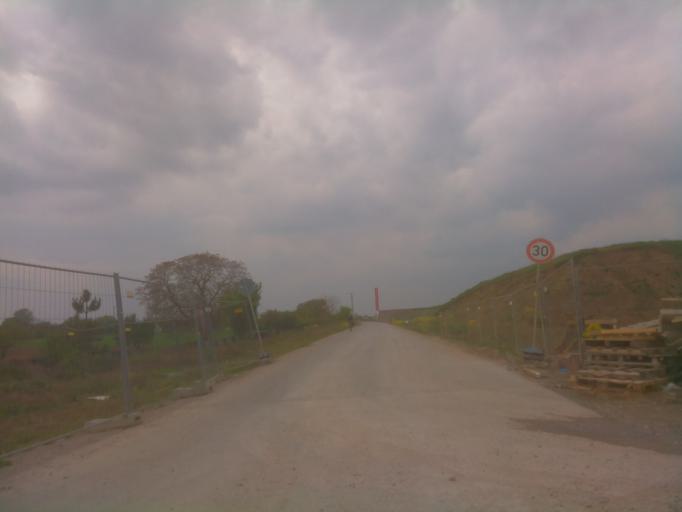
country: DE
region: Baden-Wuerttemberg
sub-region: Karlsruhe Region
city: Eppelheim
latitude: 49.4034
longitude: 8.6612
